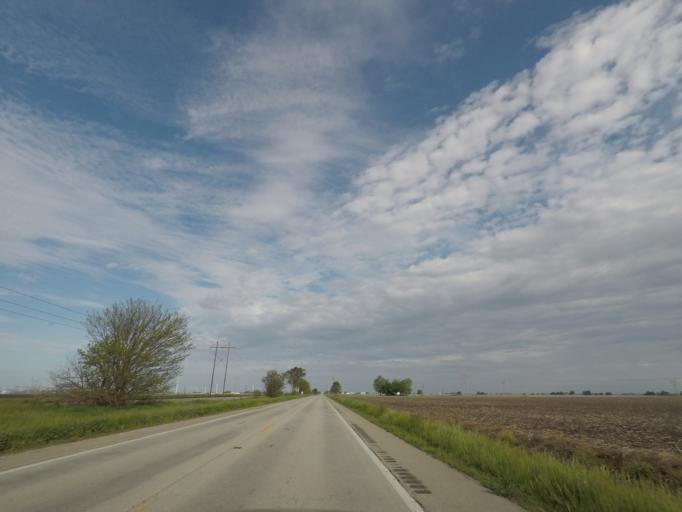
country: US
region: Illinois
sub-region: Logan County
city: Mount Pulaski
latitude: 39.9726
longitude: -89.1830
